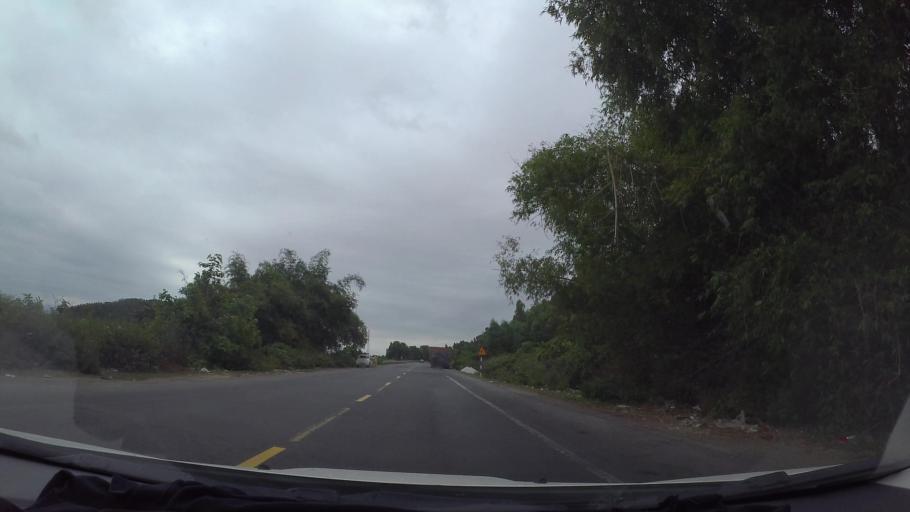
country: VN
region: Da Nang
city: Lien Chieu
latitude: 16.1211
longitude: 108.1014
